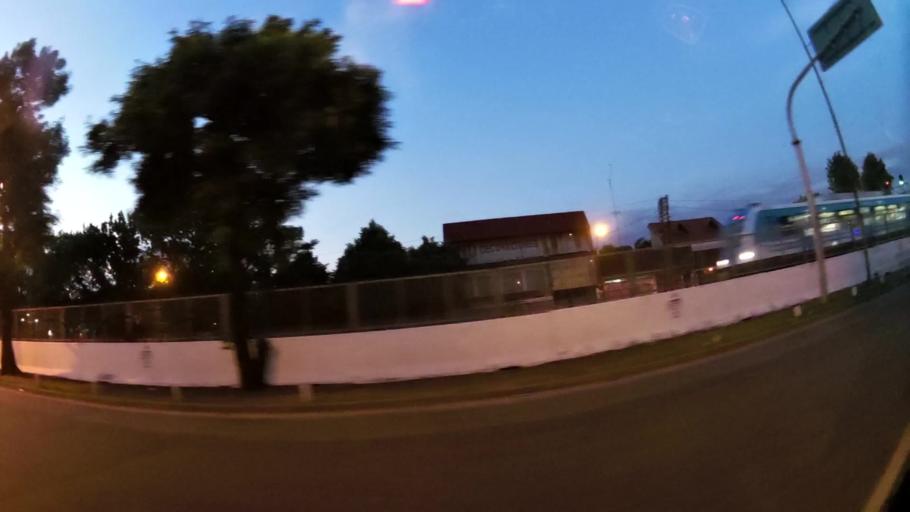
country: AR
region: Buenos Aires
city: Ituzaingo
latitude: -34.6581
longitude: -58.6608
